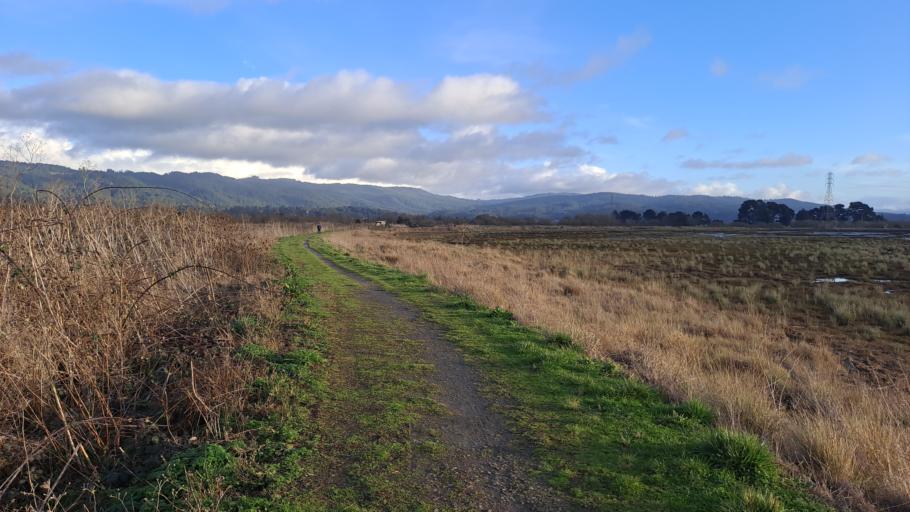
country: US
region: California
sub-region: Humboldt County
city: Arcata
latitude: 40.8642
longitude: -124.0989
